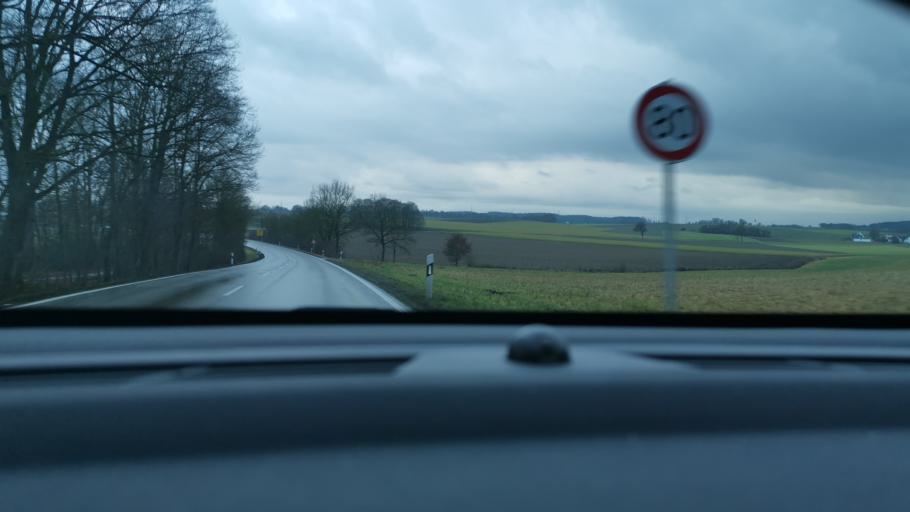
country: DE
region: Bavaria
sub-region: Swabia
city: Petersdorf
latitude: 48.4964
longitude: 11.0130
